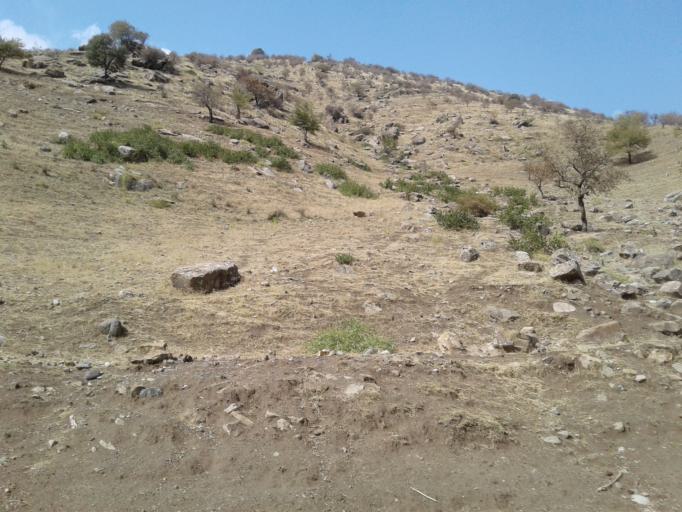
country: TJ
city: Shahrinav
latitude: 38.6703
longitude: 68.3524
